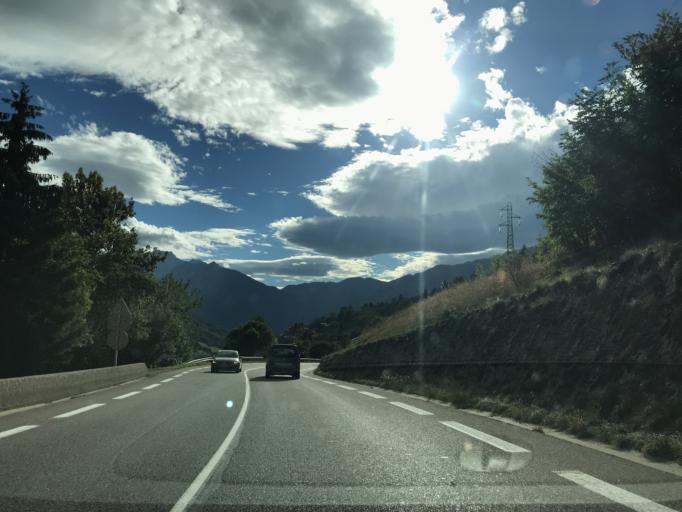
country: FR
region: Rhone-Alpes
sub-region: Departement de la Haute-Savoie
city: Saint-Jean-de-Sixt
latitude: 45.9186
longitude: 6.3824
